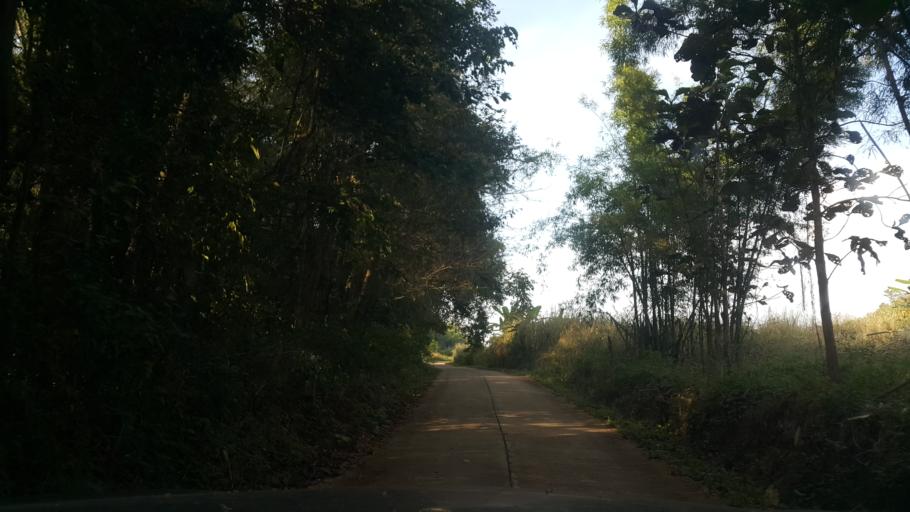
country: TH
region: Chiang Mai
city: Samoeng
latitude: 18.9803
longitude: 98.6837
